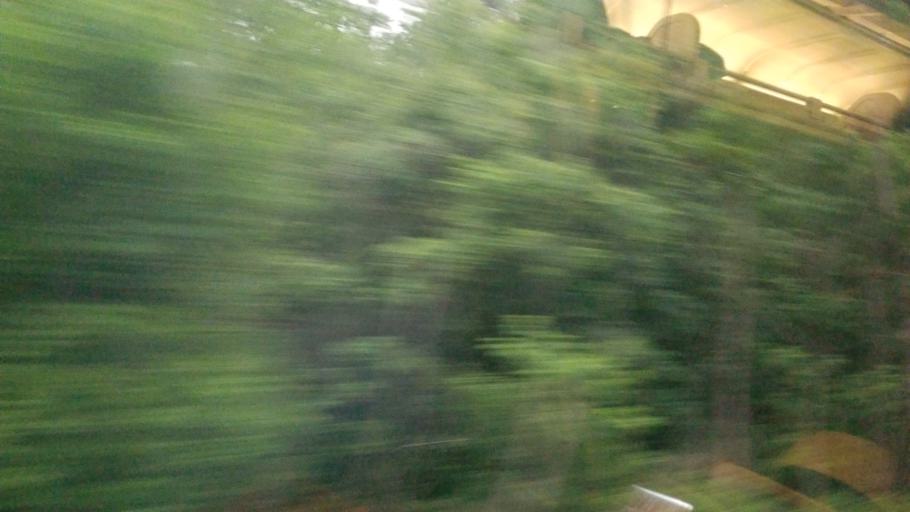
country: US
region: Virginia
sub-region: Orange County
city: Orange
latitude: 38.2833
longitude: -78.0919
